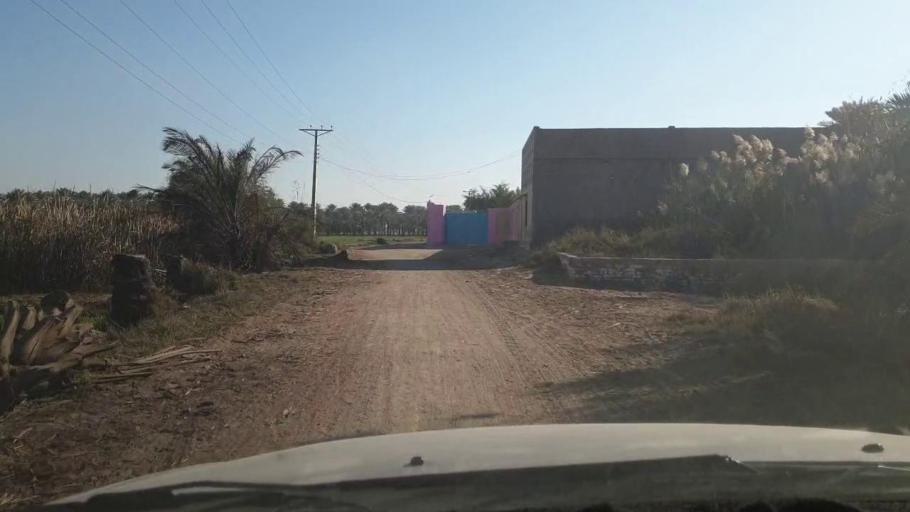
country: PK
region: Sindh
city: Ghotki
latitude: 28.0576
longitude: 69.3238
